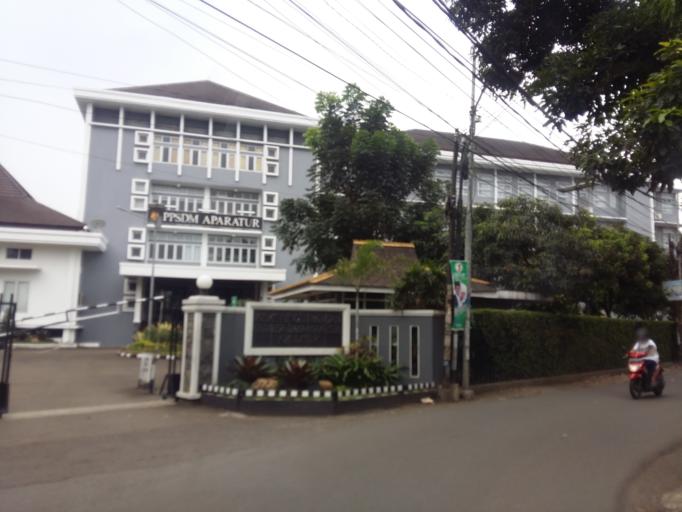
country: ID
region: West Java
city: Bandung
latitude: -6.8797
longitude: 107.6121
